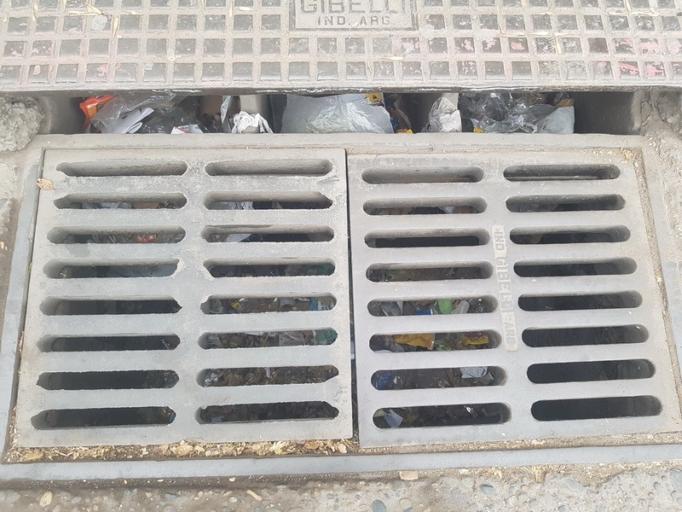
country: AR
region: Neuquen
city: Neuquen
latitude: -38.9593
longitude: -68.0596
